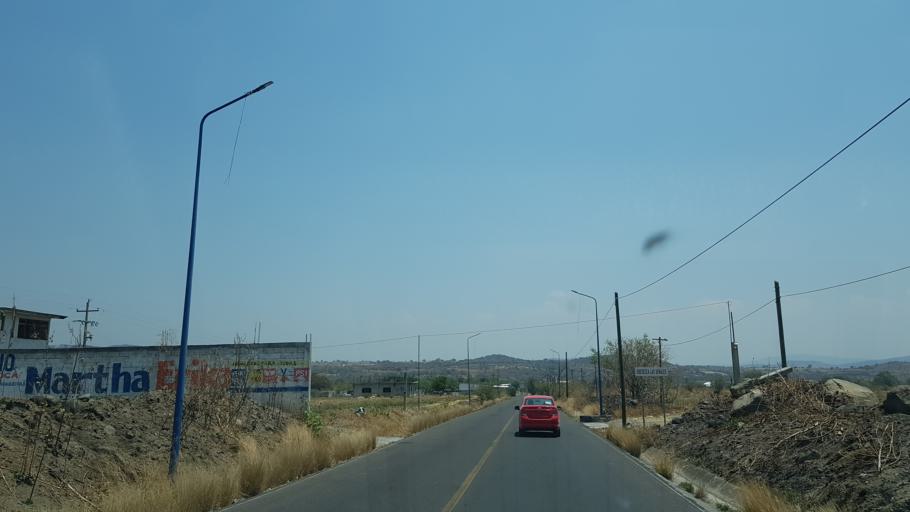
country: MX
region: Puebla
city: Huaquechula
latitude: 18.7653
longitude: -98.5308
